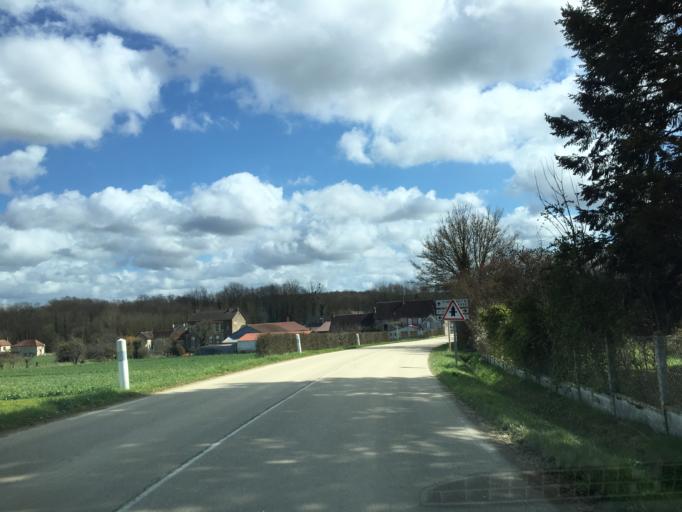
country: FR
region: Bourgogne
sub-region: Departement de l'Yonne
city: Aillant-sur-Tholon
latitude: 47.8446
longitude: 3.3919
